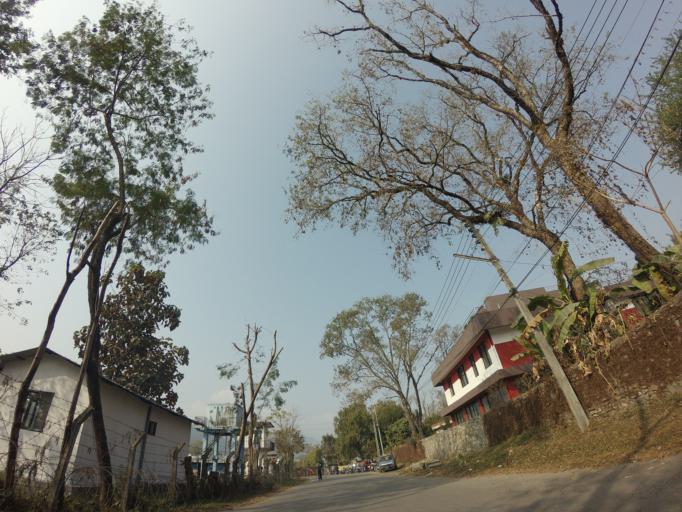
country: NP
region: Western Region
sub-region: Gandaki Zone
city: Pokhara
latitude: 28.2049
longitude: 83.9715
